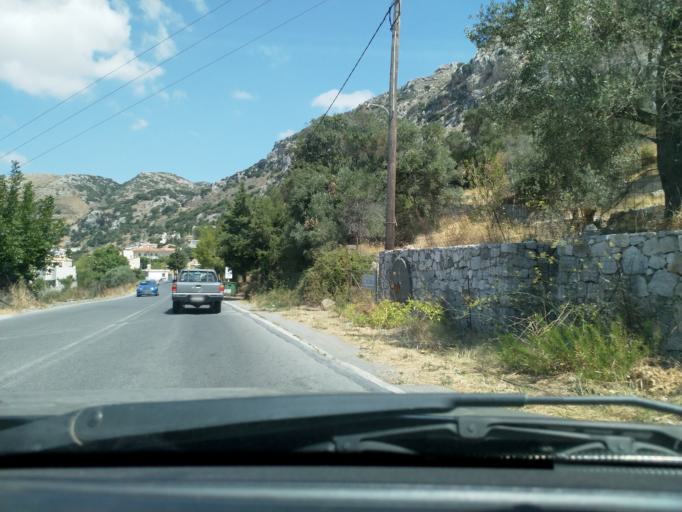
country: GR
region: Crete
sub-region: Nomos Rethymnis
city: Agia Foteini
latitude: 35.2107
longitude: 24.5349
